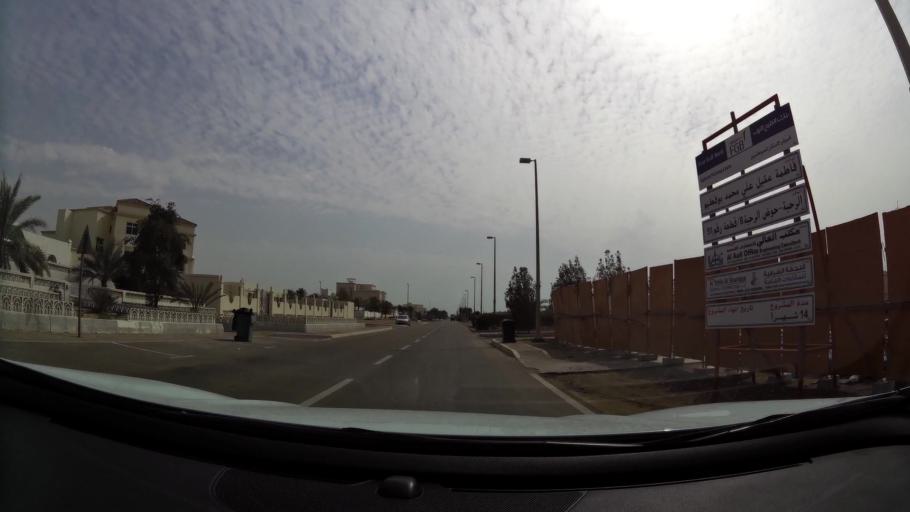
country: AE
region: Abu Dhabi
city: Abu Dhabi
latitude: 24.5720
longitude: 54.6865
